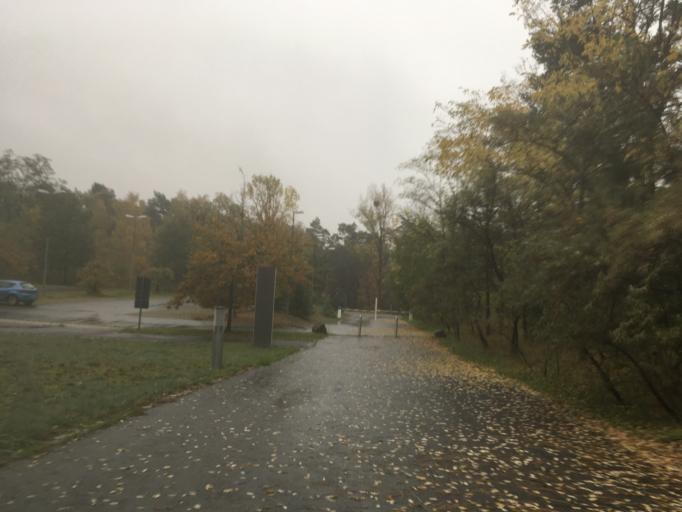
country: DE
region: Brandenburg
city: Halbe
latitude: 52.0308
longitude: 13.7409
